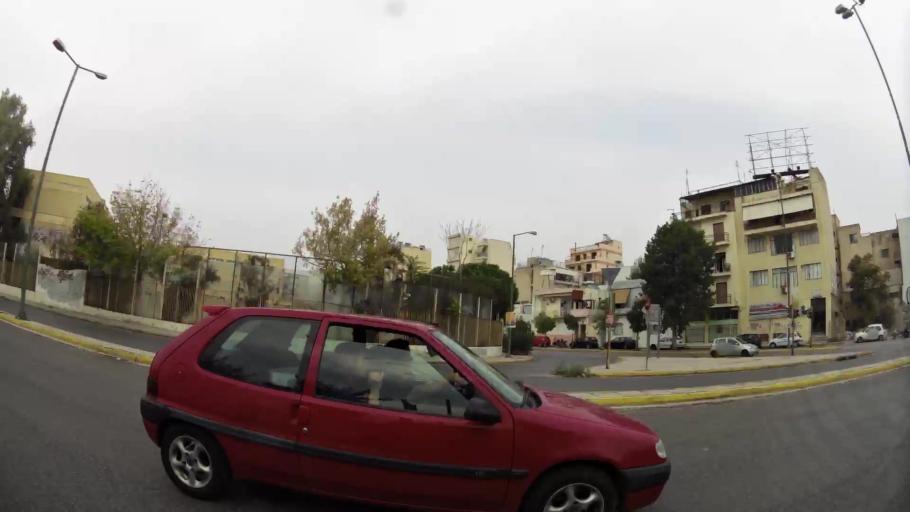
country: GR
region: Attica
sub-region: Nomarchia Athinas
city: Athens
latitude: 37.9756
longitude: 23.7041
